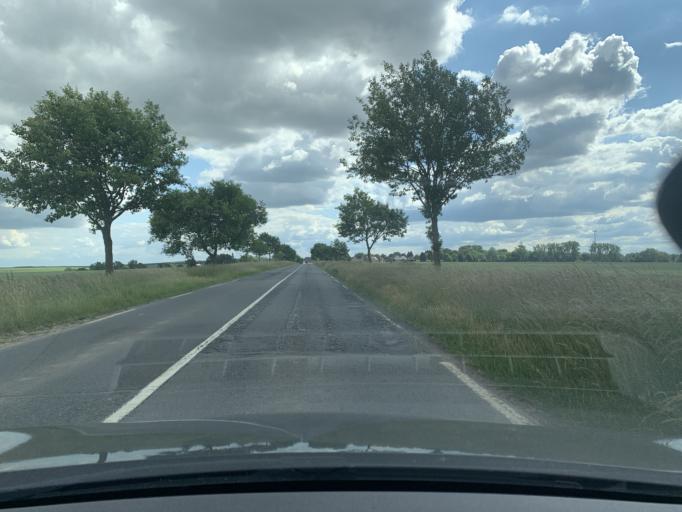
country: FR
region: Picardie
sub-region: Departement de la Somme
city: Moislains
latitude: 50.0150
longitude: 3.0290
